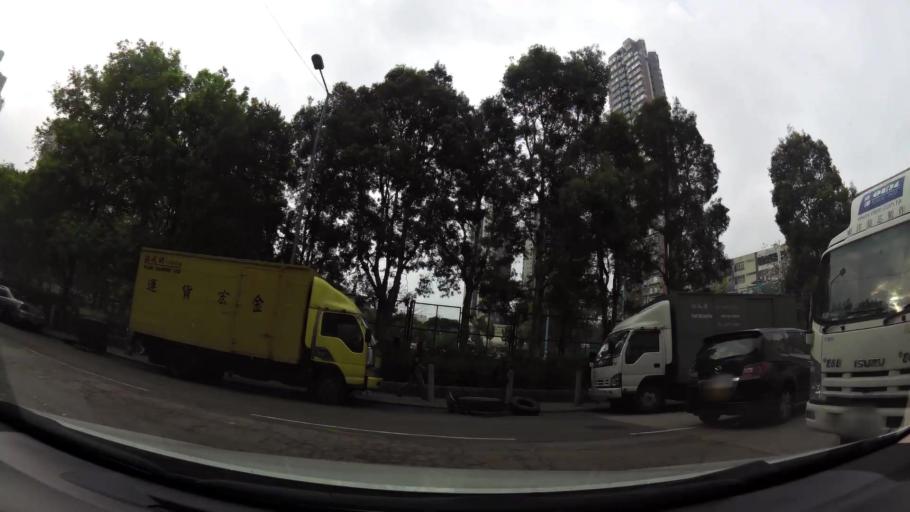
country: HK
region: Kowloon City
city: Kowloon
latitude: 22.2953
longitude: 114.2370
